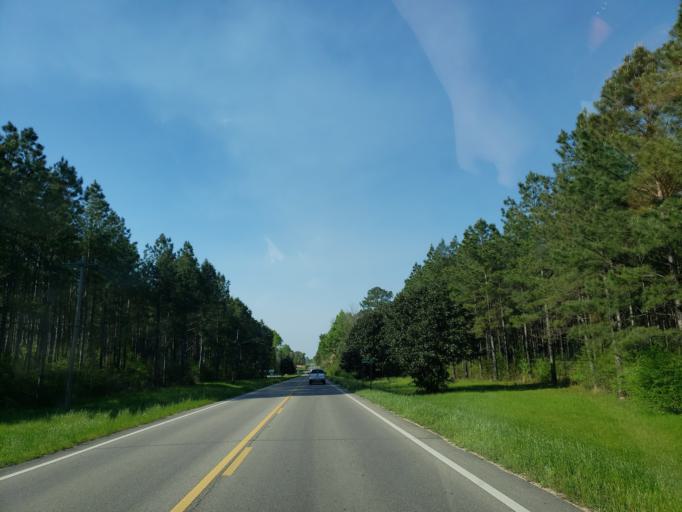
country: US
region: Mississippi
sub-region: Perry County
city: Richton
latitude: 31.3582
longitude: -88.9354
